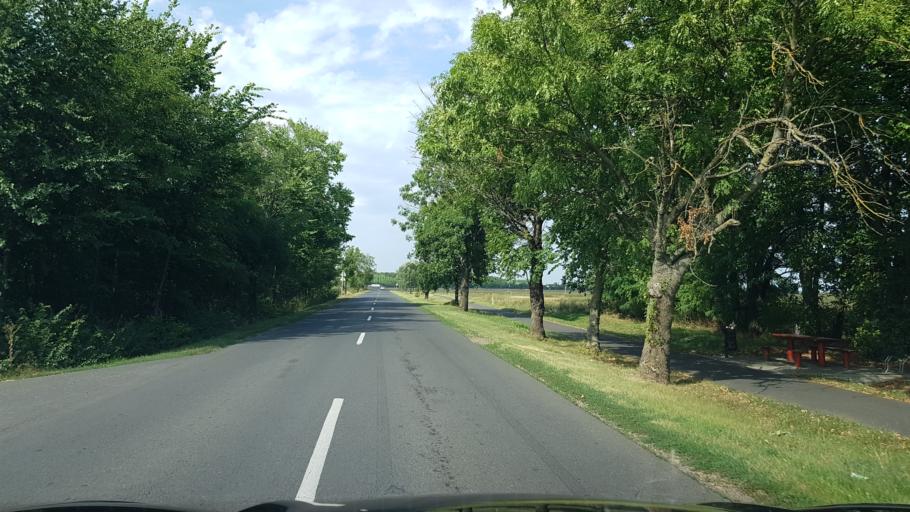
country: HU
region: Bekes
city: Fuzesgyarmat
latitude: 47.0667
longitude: 21.1956
